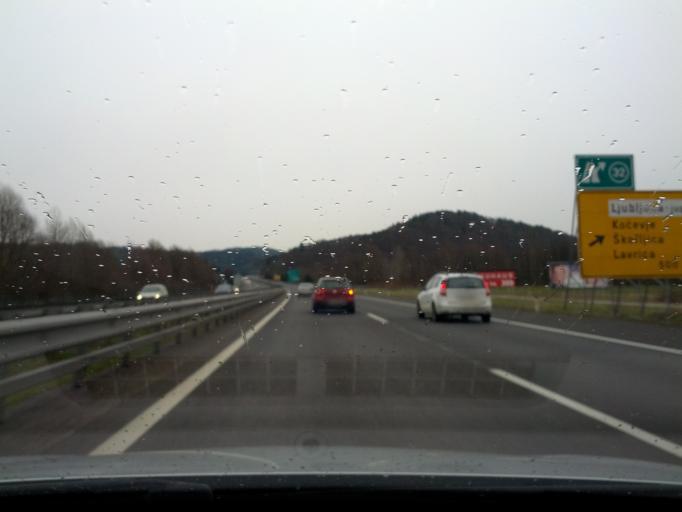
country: SI
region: Skofljica
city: Lavrica
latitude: 46.0154
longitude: 14.5326
